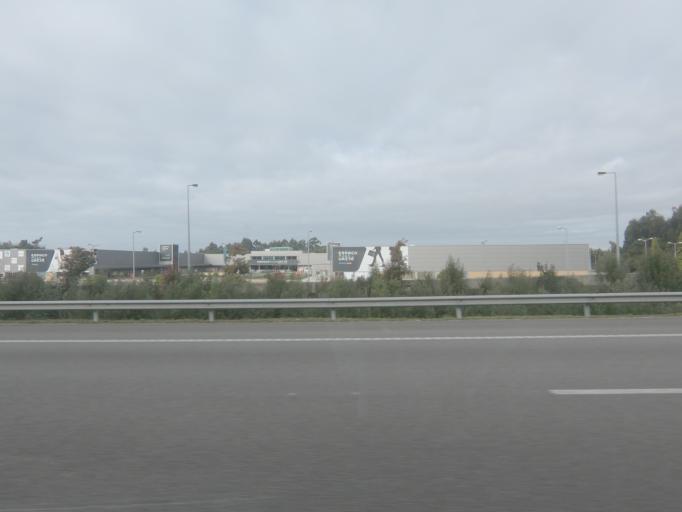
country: PT
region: Porto
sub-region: Vila Nova de Gaia
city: Grijo
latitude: 41.0390
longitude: -8.5703
